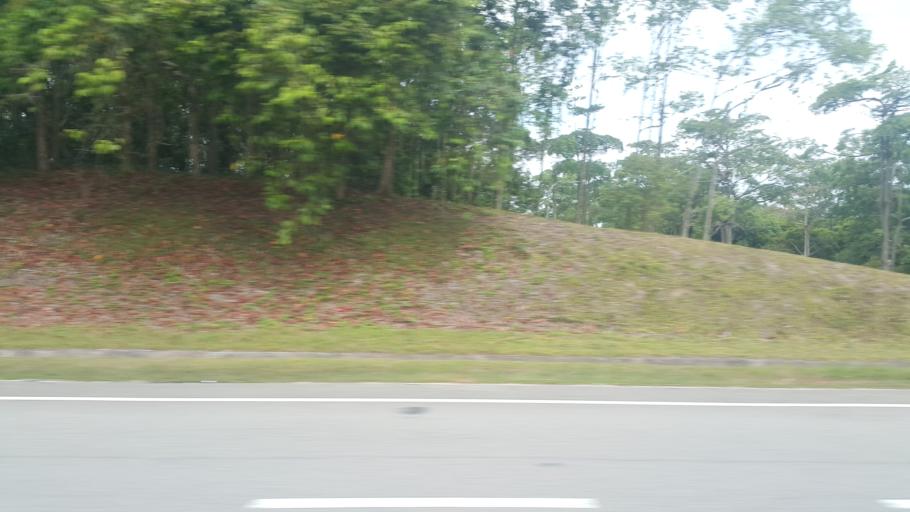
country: MY
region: Johor
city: Skudai
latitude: 1.4315
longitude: 103.6049
